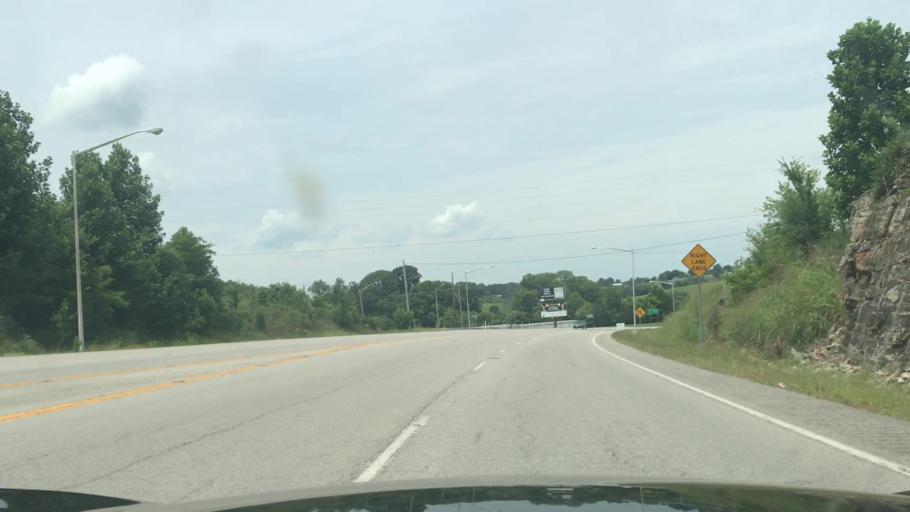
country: US
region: Kentucky
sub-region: Green County
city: Greensburg
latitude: 37.2735
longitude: -85.5069
